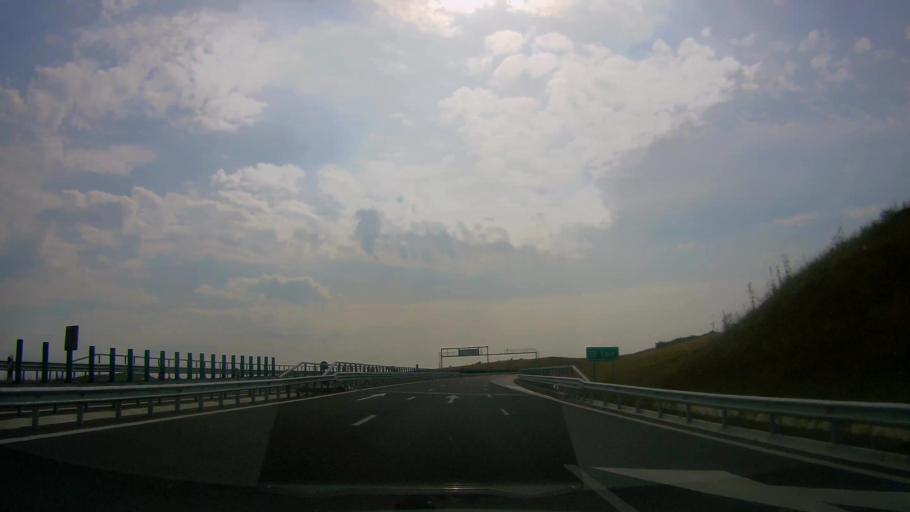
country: RO
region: Cluj
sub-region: Comuna Baciu
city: Mera
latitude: 46.8051
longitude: 23.4260
